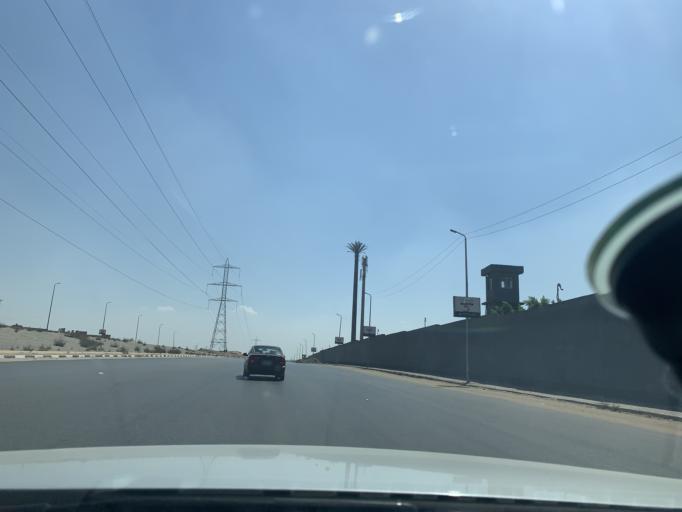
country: EG
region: Muhafazat al Qahirah
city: Cairo
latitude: 30.0342
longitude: 31.3530
